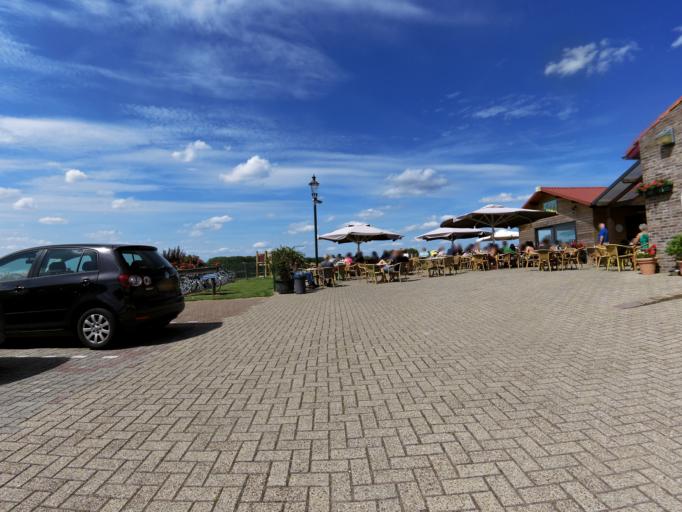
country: NL
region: Limburg
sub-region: Gemeente Schinnen
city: Puth
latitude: 50.9731
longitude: 5.8832
